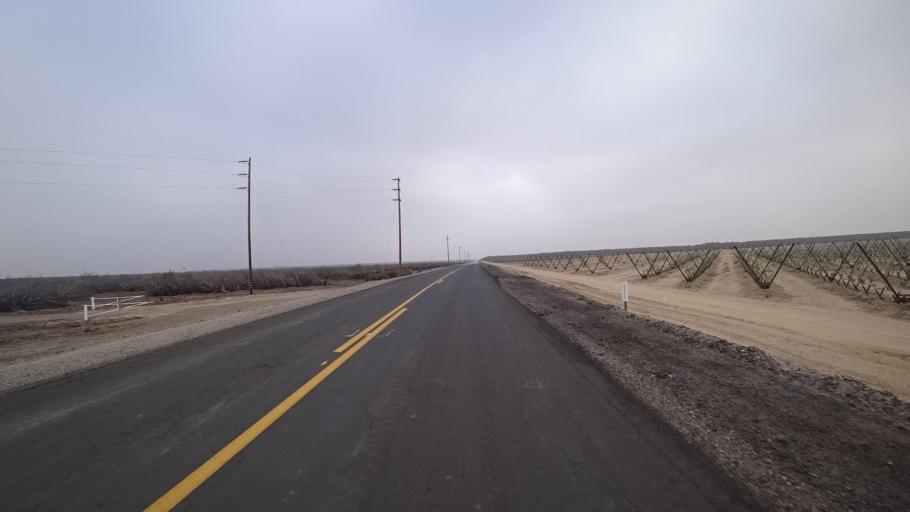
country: US
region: California
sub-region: Kern County
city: Maricopa
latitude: 35.1133
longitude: -119.3504
